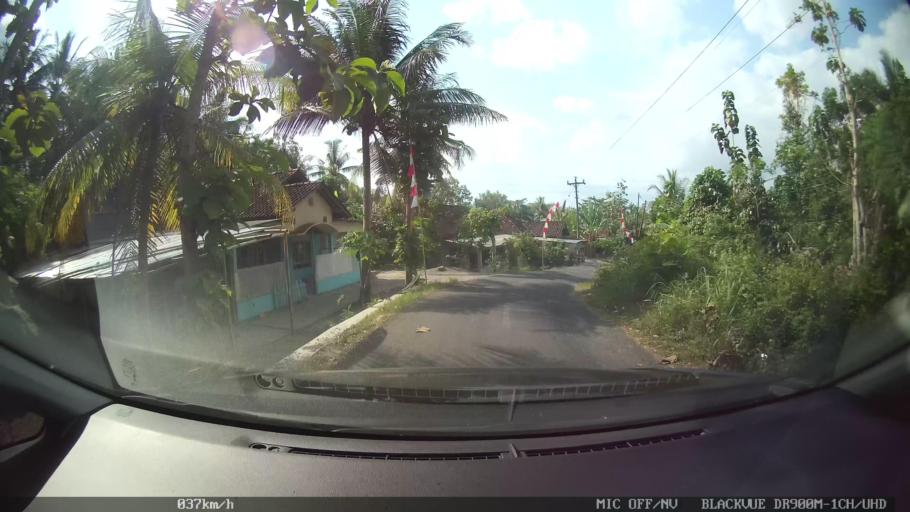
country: ID
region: Daerah Istimewa Yogyakarta
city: Kasihan
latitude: -7.8489
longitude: 110.3001
